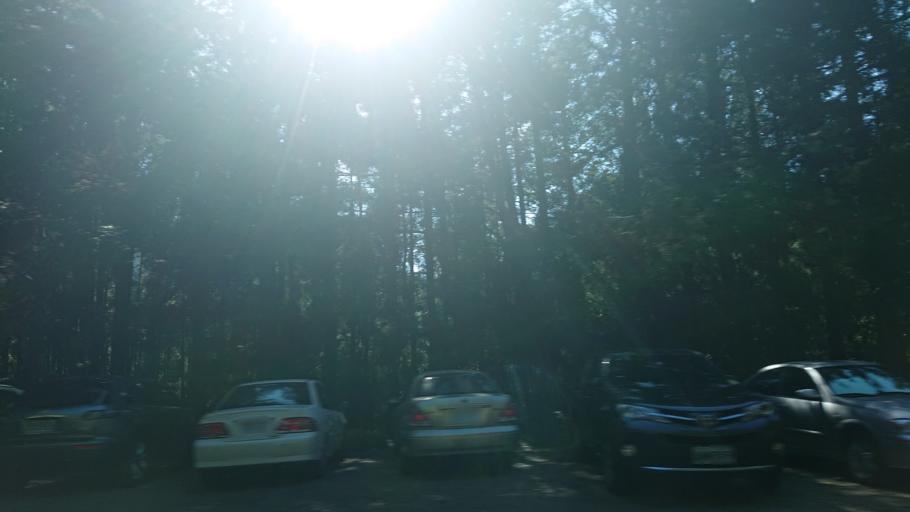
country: TW
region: Taiwan
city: Lugu
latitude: 23.4856
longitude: 120.8292
